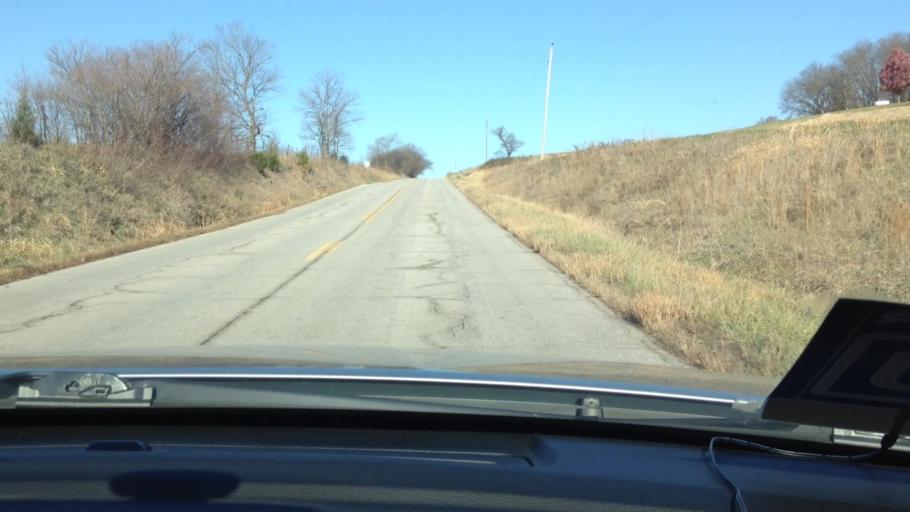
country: US
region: Missouri
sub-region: Platte County
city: Weston
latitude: 39.4734
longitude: -94.9007
